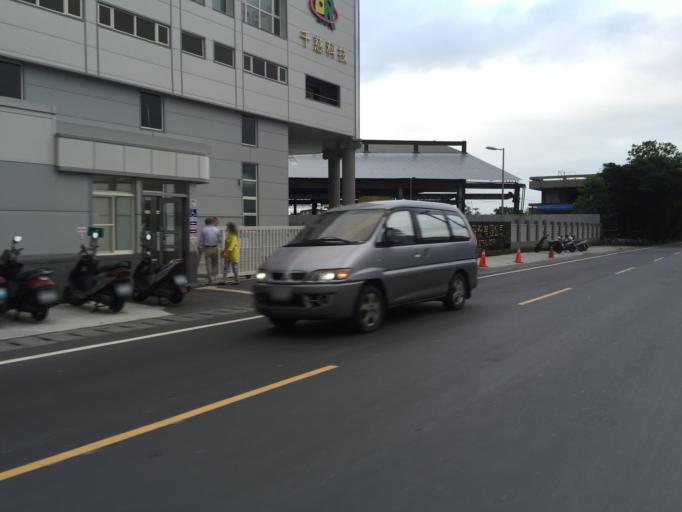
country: TW
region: Taiwan
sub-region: Yilan
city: Yilan
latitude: 24.7807
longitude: 121.7343
